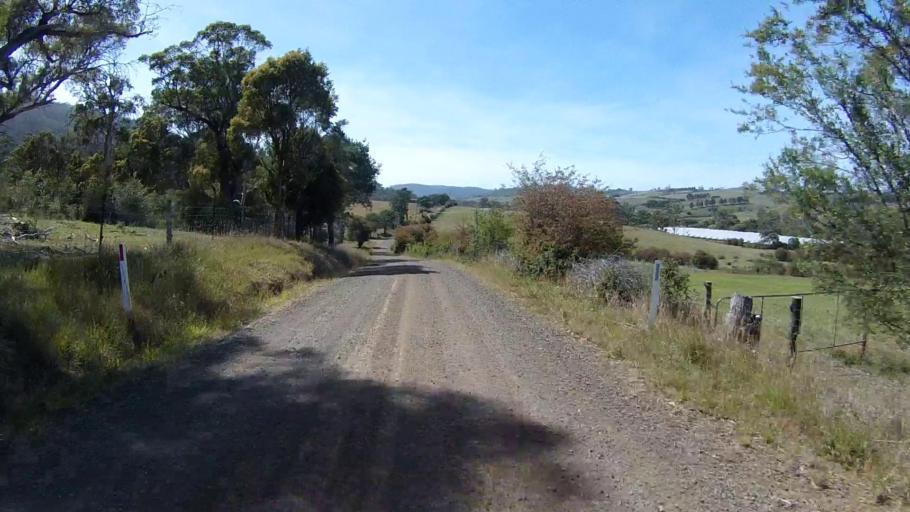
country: AU
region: Tasmania
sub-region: Sorell
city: Sorell
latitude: -42.7473
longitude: 147.6169
